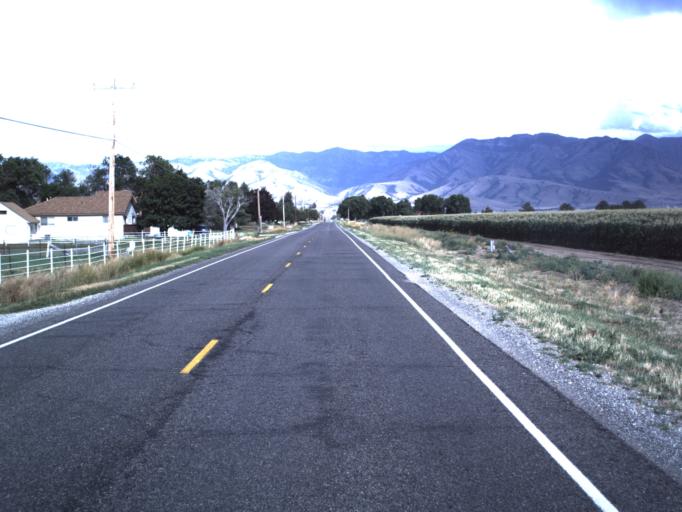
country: US
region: Utah
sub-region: Cache County
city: Lewiston
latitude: 41.9755
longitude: -111.9042
